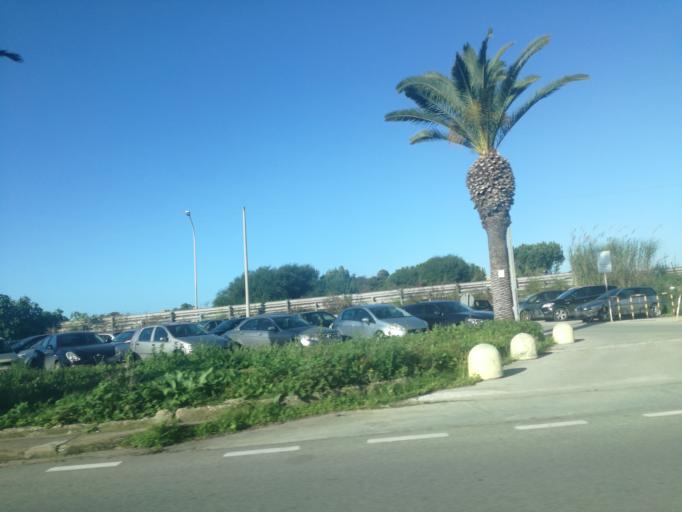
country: IT
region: Sicily
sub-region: Provincia di Caltanissetta
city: Gela
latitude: 37.0605
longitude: 14.2657
